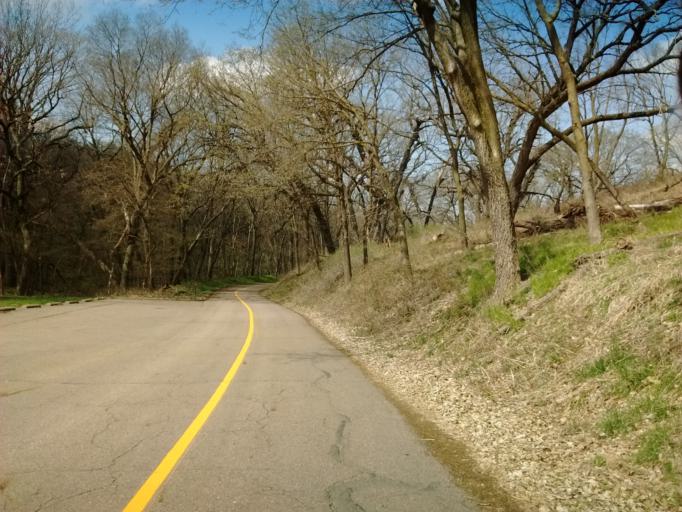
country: US
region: South Dakota
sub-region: Union County
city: North Sioux City
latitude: 42.5559
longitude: -96.4650
